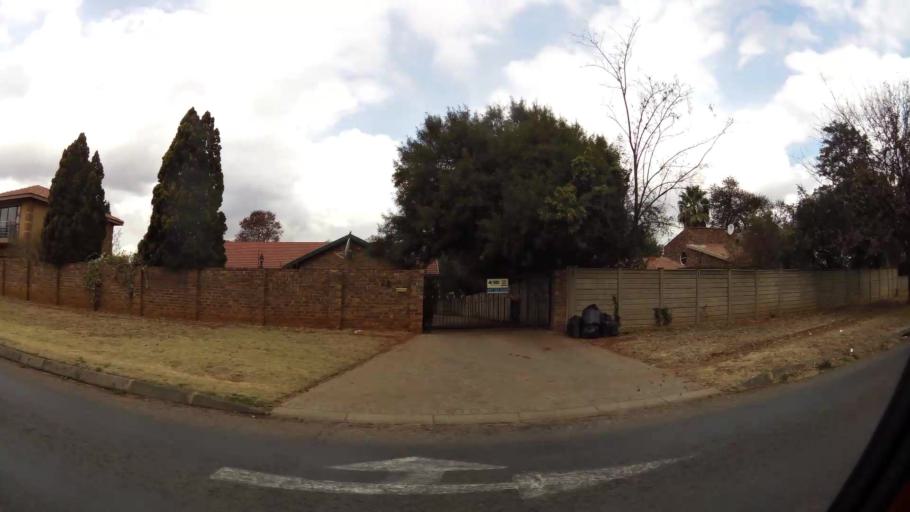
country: ZA
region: Gauteng
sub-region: Sedibeng District Municipality
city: Vanderbijlpark
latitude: -26.7325
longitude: 27.8462
